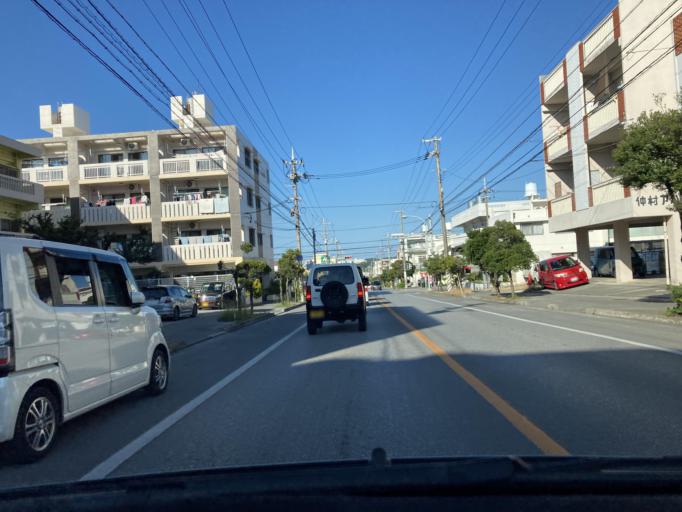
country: JP
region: Okinawa
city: Ginowan
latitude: 26.2808
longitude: 127.7814
